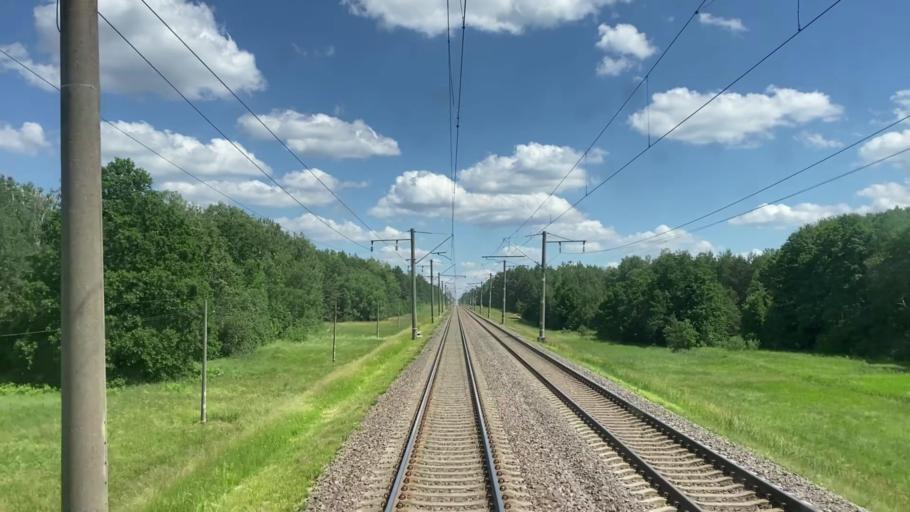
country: BY
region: Brest
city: Ivatsevichy
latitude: 52.8475
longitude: 25.5640
